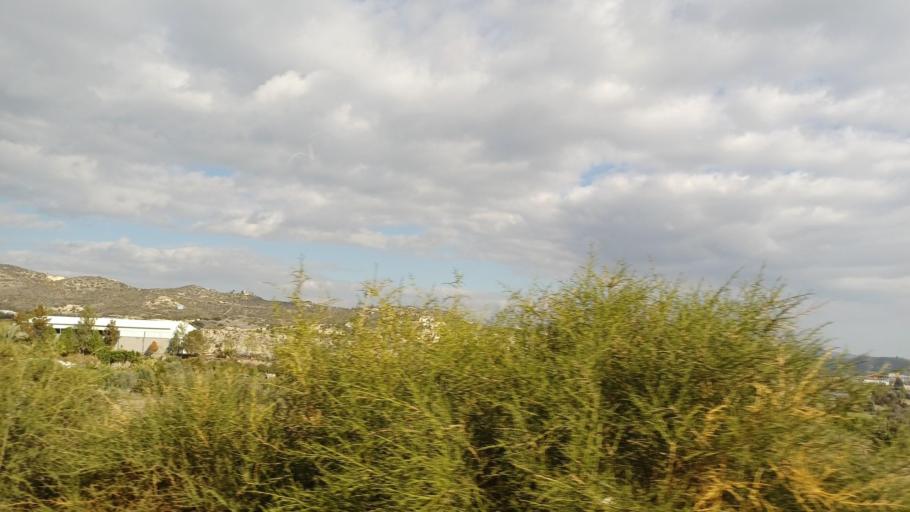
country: CY
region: Larnaka
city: Kofinou
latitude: 34.8127
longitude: 33.3502
